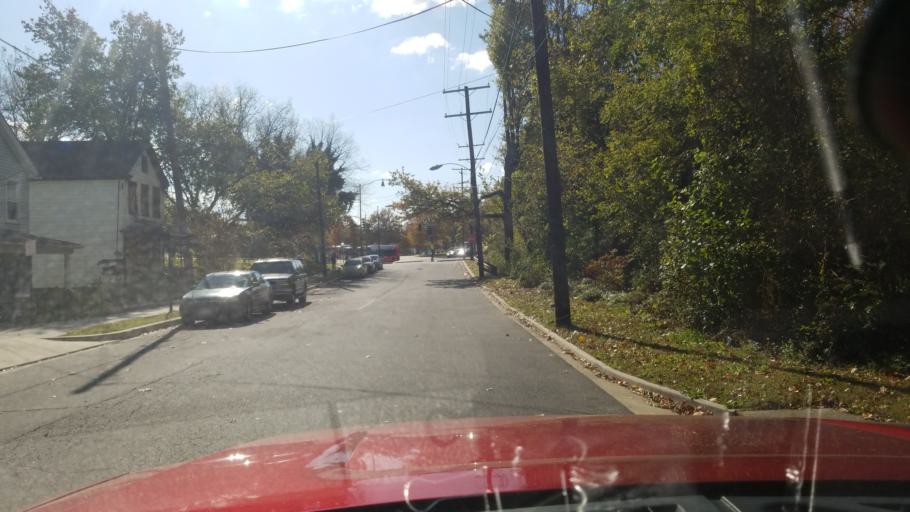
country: US
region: Maryland
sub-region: Prince George's County
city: Capitol Heights
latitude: 38.8907
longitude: -76.9137
